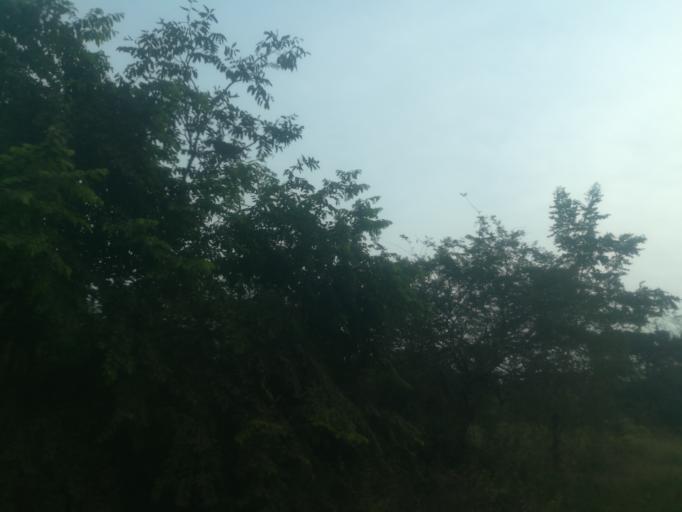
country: NG
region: Ogun
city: Abeokuta
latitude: 7.1967
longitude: 3.2279
